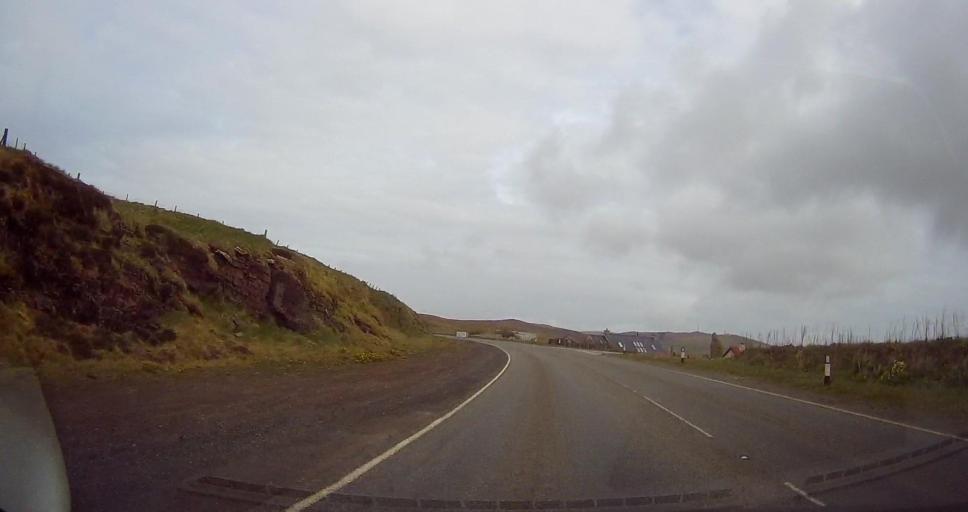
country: GB
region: Scotland
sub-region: Shetland Islands
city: Lerwick
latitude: 60.1201
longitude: -1.2150
